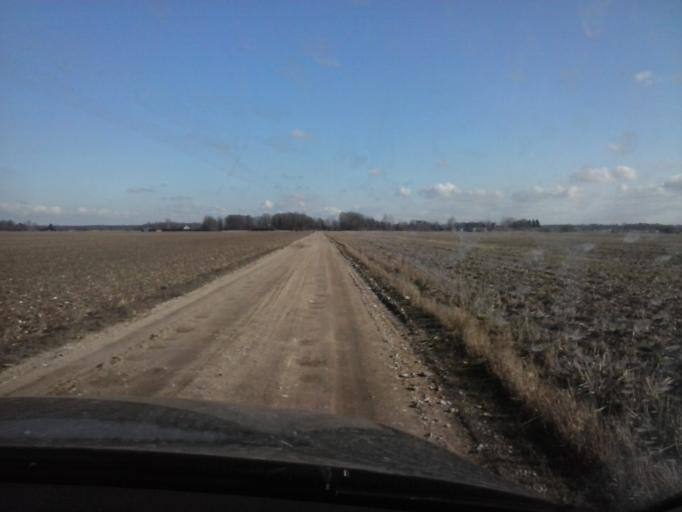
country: EE
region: Tartu
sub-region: Puhja vald
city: Puhja
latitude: 58.2849
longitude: 26.1515
